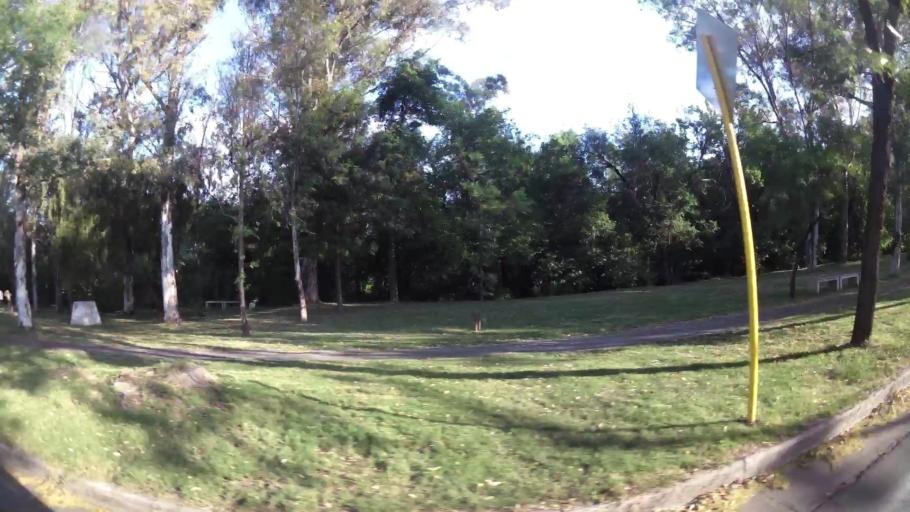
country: AR
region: Cordoba
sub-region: Departamento de Capital
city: Cordoba
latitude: -31.3942
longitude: -64.2185
